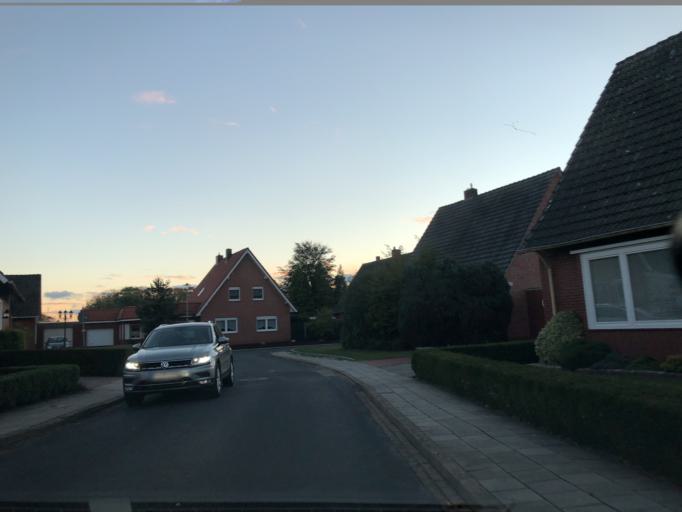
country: DE
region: Lower Saxony
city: Papenburg
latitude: 53.0786
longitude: 7.4139
